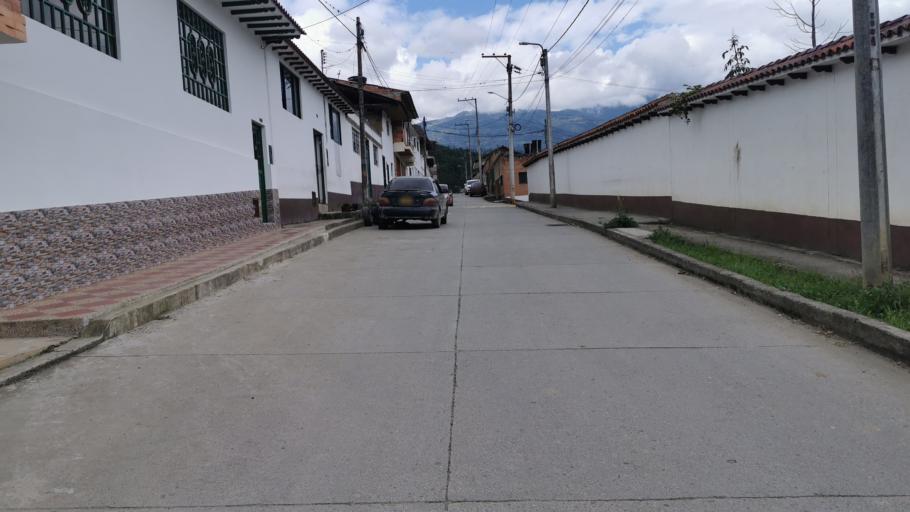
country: CO
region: Cundinamarca
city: Tenza
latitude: 5.0763
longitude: -73.4216
